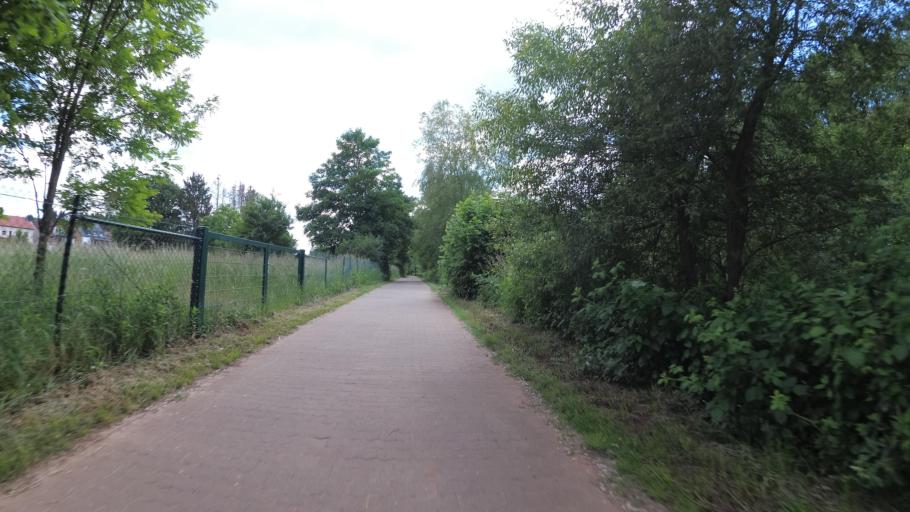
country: DE
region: Saarland
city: Puttlingen
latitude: 49.3066
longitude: 6.9009
